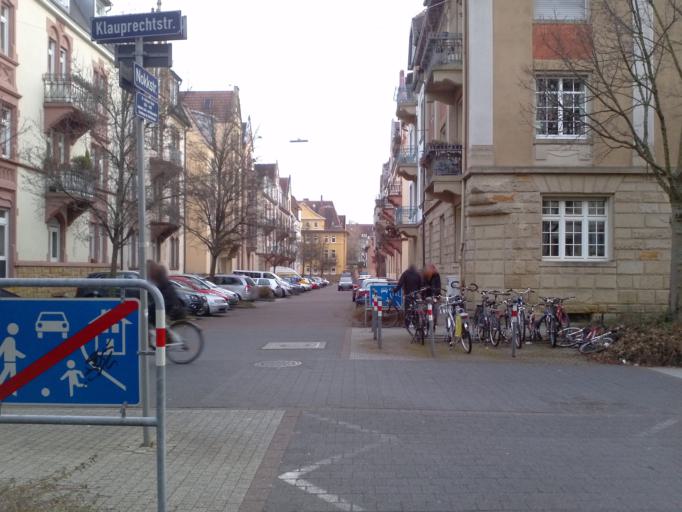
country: DE
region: Baden-Wuerttemberg
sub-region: Karlsruhe Region
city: Karlsruhe
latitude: 49.0012
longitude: 8.3874
